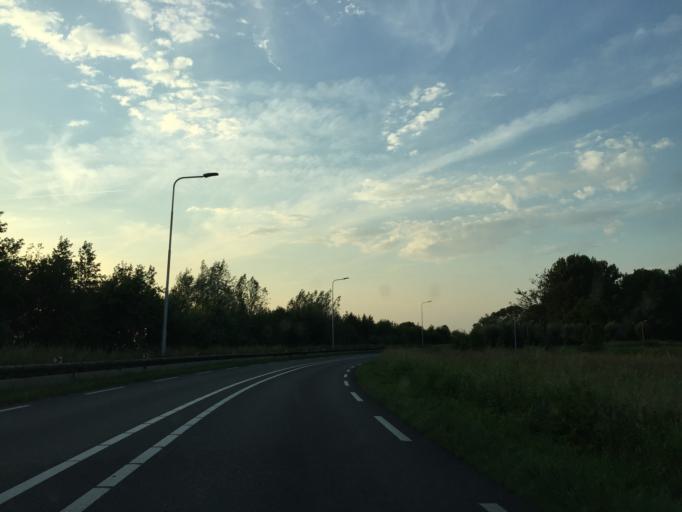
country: NL
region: South Holland
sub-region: Gemeente Vlist
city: Haastrecht
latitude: 51.9875
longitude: 4.7503
